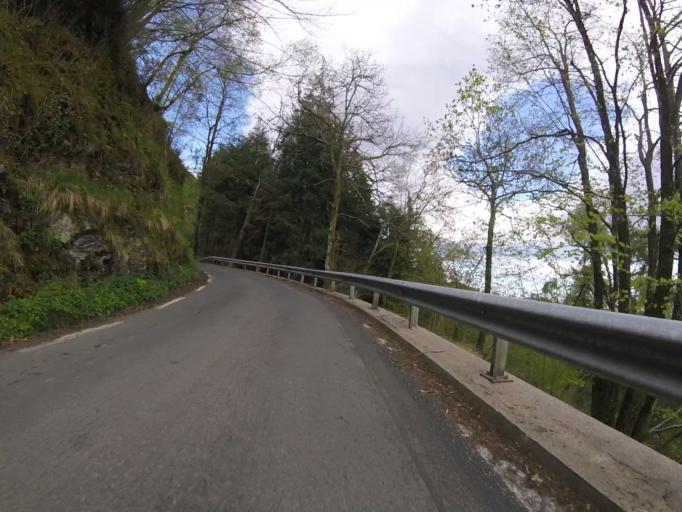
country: ES
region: Basque Country
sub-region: Provincia de Guipuzcoa
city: Errezil
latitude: 43.2015
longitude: -2.1962
